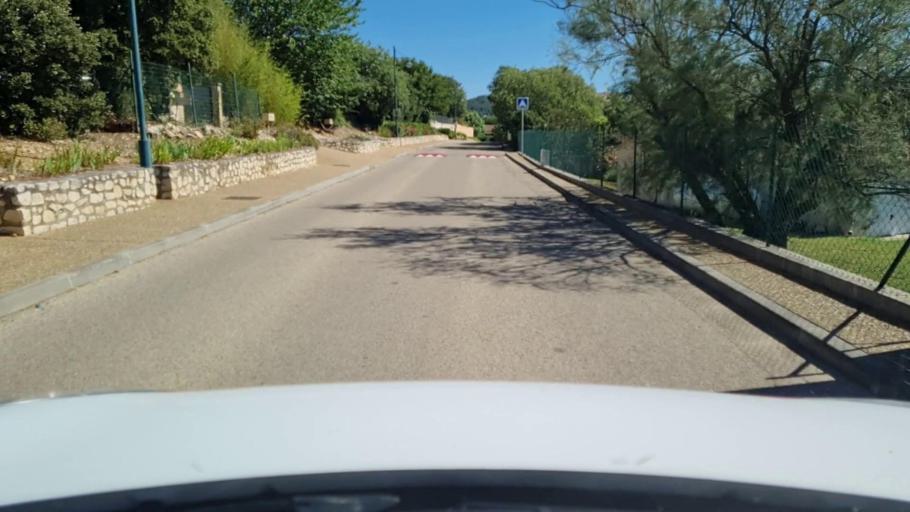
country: FR
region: Languedoc-Roussillon
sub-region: Departement du Gard
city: Villevieille
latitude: 43.8506
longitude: 4.1084
